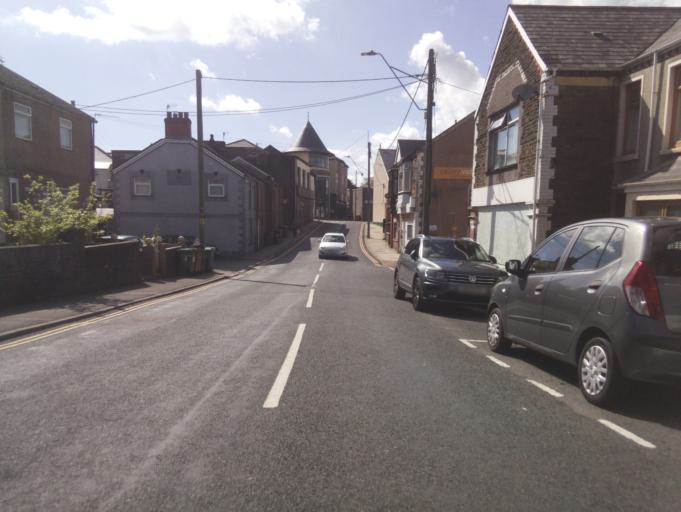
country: GB
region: Wales
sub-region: Caerphilly County Borough
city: Caerphilly
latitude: 51.5741
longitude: -3.2166
